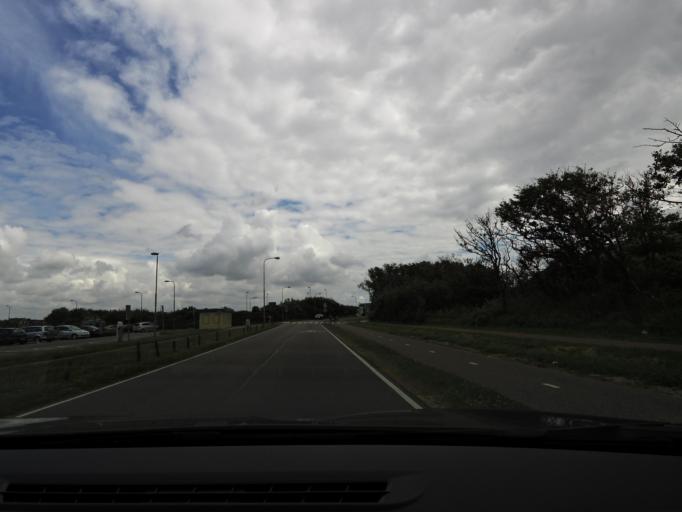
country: NL
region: Zeeland
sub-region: Gemeente Vlissingen
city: Vlissingen
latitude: 51.5035
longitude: 3.4773
